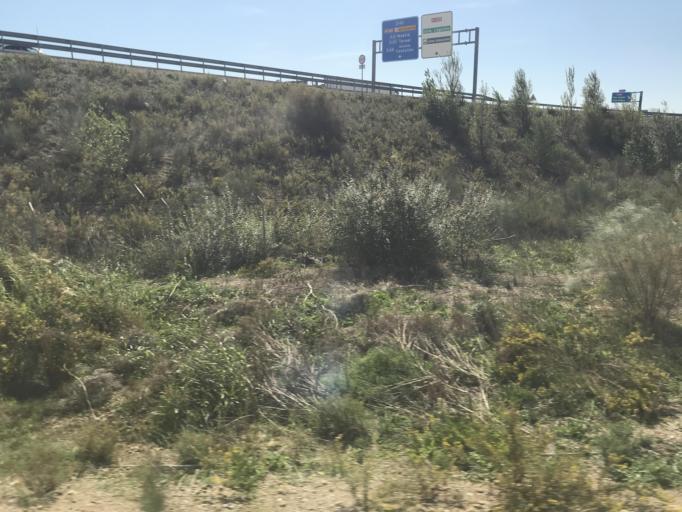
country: ES
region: Aragon
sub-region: Provincia de Zaragoza
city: Oliver-Valdefierro, Oliver, Valdefierro
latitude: 41.6698
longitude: -0.9352
